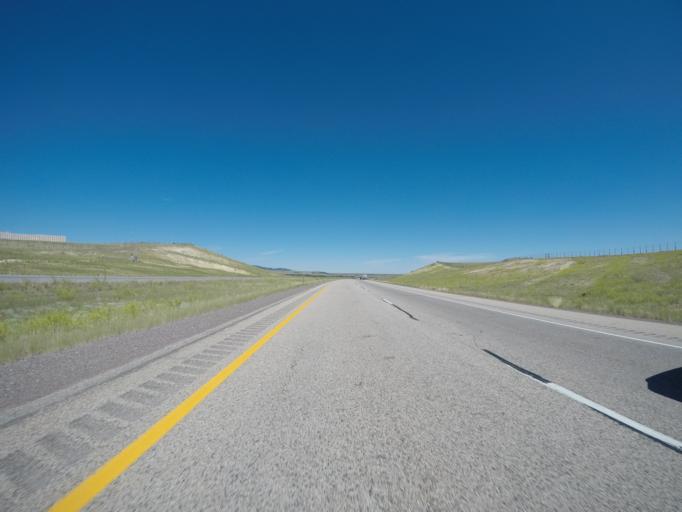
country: US
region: Wyoming
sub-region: Albany County
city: Laramie
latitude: 41.4955
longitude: -106.0445
